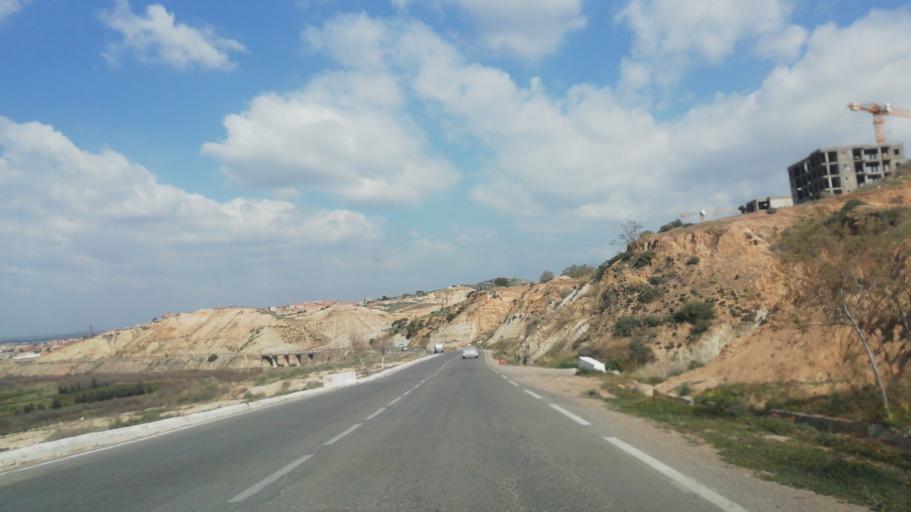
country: DZ
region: Mascara
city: Mascara
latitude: 35.5589
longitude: 0.0679
